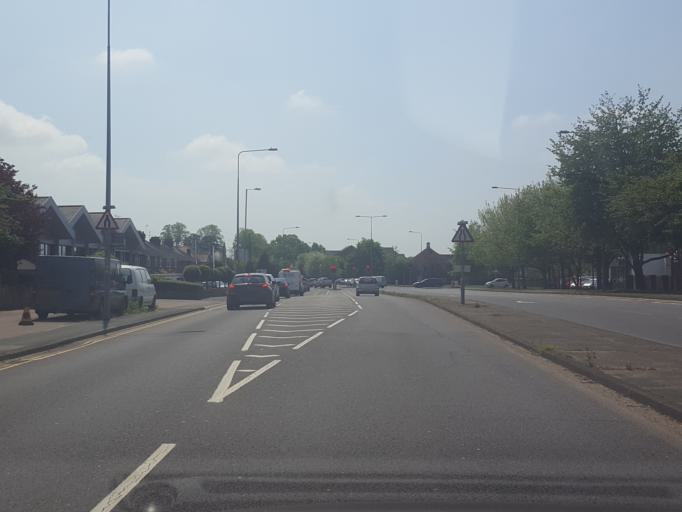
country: GB
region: England
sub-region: Essex
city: Colchester
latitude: 51.9147
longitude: 0.9296
